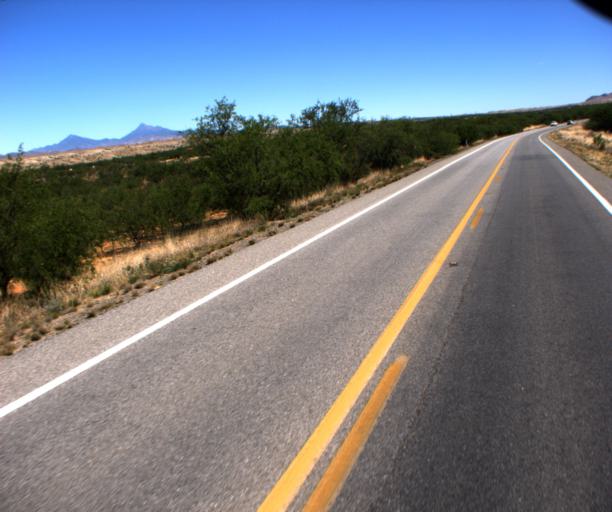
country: US
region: Arizona
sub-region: Santa Cruz County
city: Nogales
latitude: 31.4063
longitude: -110.8655
